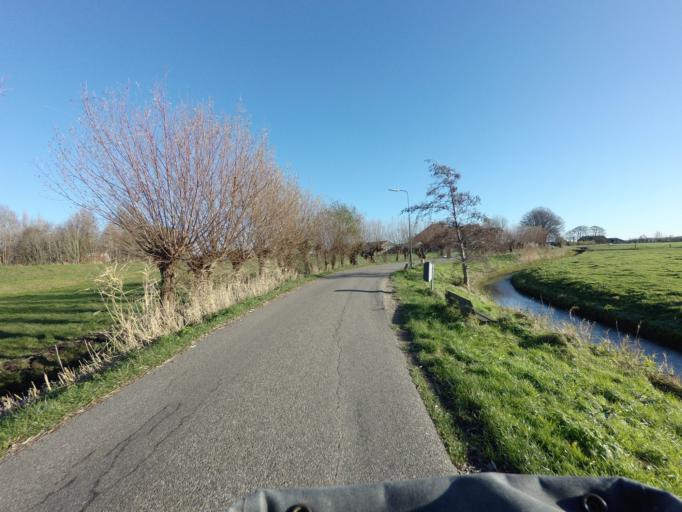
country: NL
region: North Holland
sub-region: Gemeente Amsterdam
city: Amsterdam-Zuidoost
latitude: 52.2597
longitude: 4.9776
